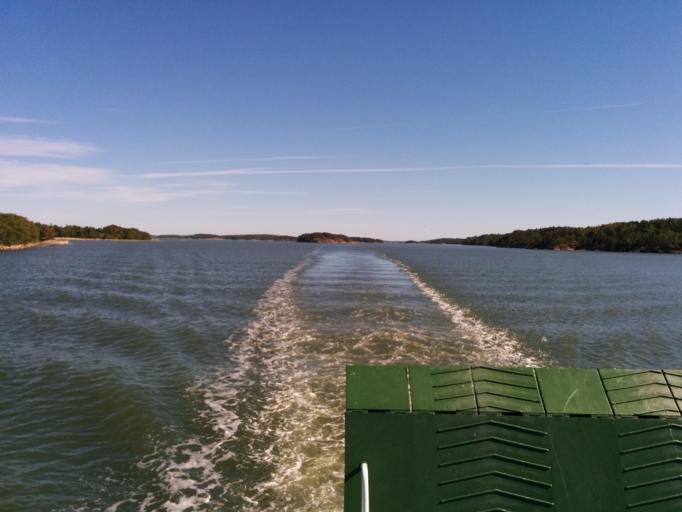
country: FI
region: Varsinais-Suomi
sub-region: Turku
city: Velkua
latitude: 60.4543
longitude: 21.7029
